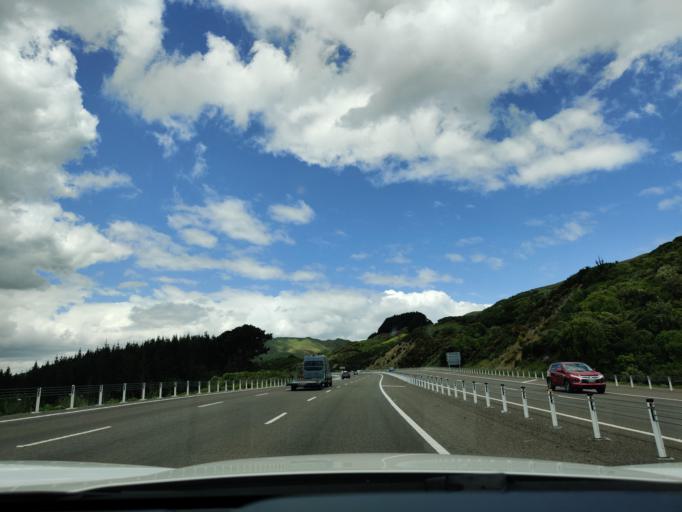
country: NZ
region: Wellington
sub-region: Porirua City
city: Porirua
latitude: -41.1511
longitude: 174.8566
